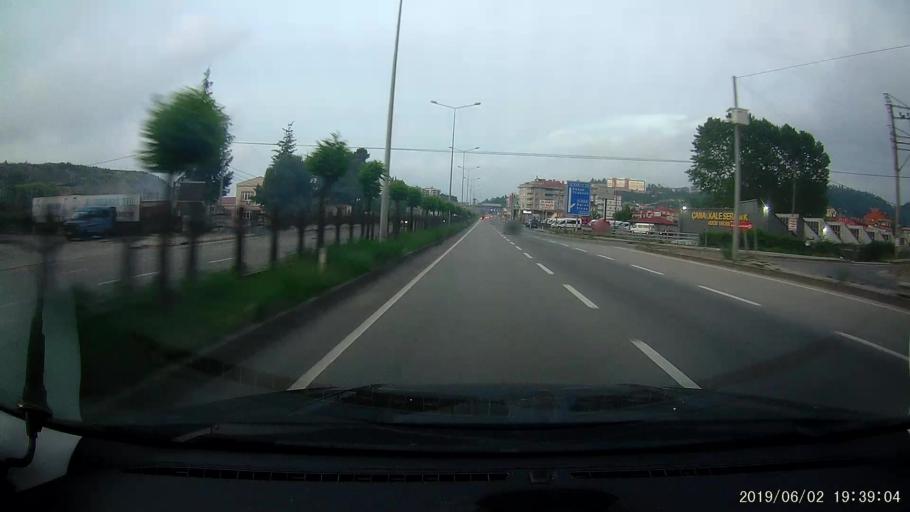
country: TR
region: Giresun
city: Giresun
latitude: 40.9116
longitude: 38.4334
